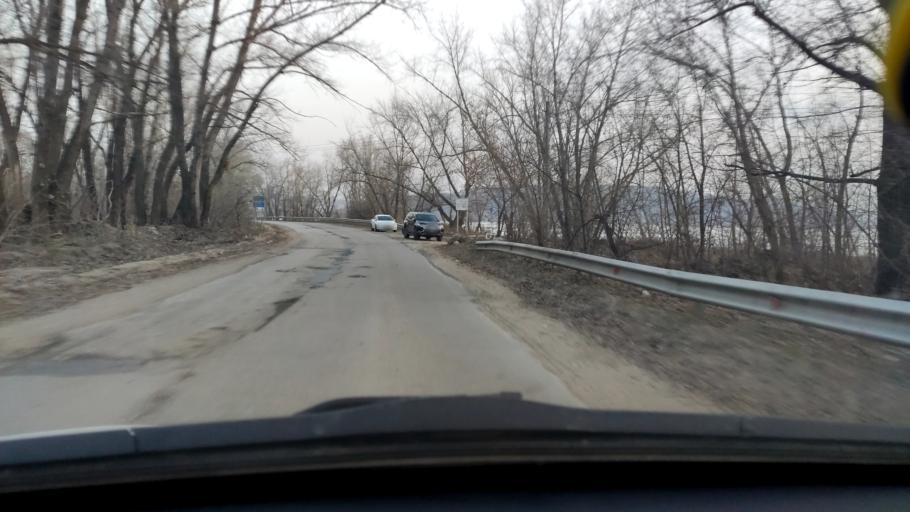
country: RU
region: Samara
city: Zhigulevsk
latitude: 53.4607
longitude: 49.5086
